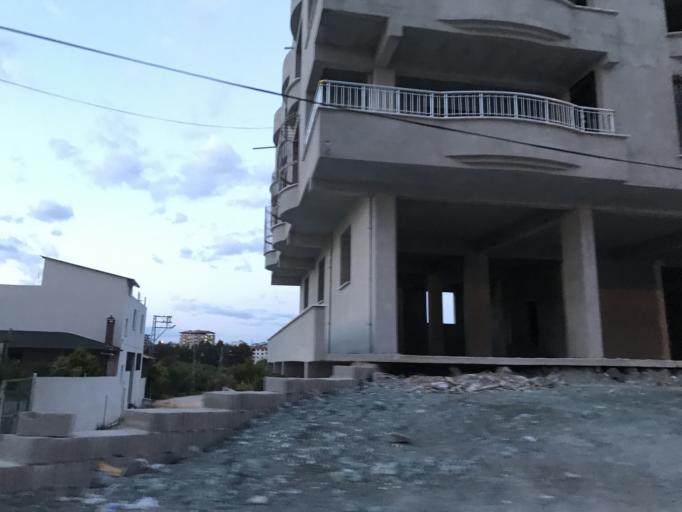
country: TR
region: Hatay
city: Uzunbag
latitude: 36.1330
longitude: 36.0410
